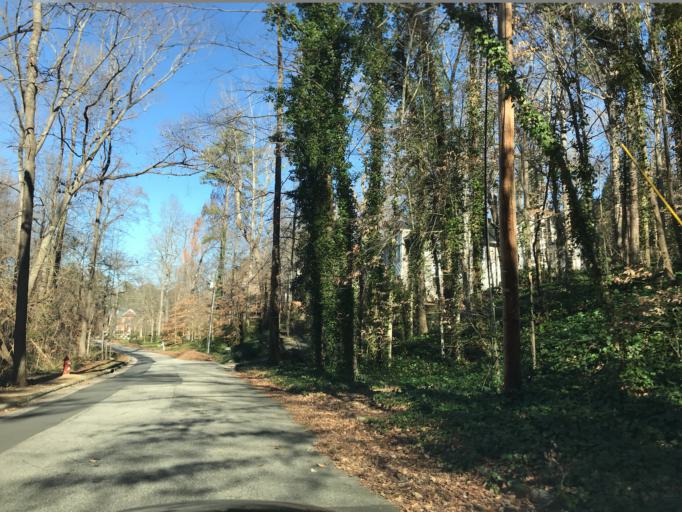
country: US
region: North Carolina
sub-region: Wake County
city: West Raleigh
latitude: 35.8170
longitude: -78.6453
